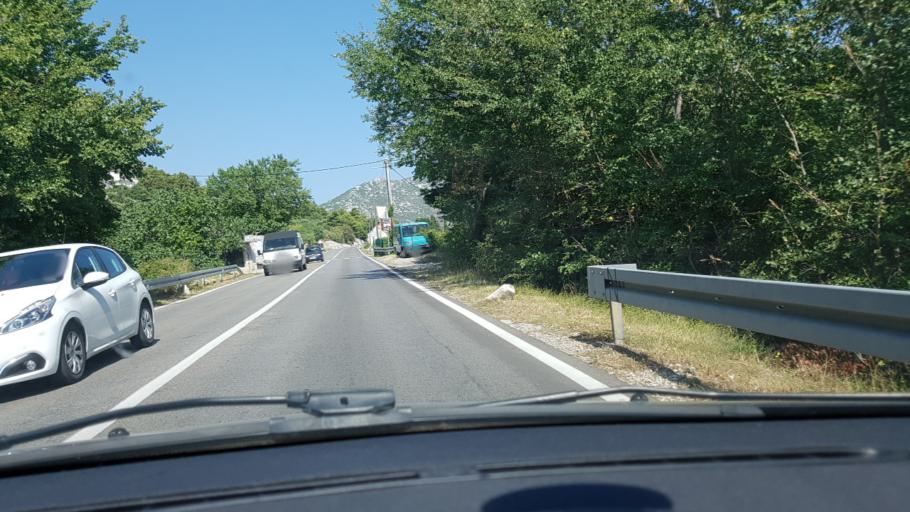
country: HR
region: Splitsko-Dalmatinska
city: Klis
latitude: 43.5564
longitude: 16.5117
